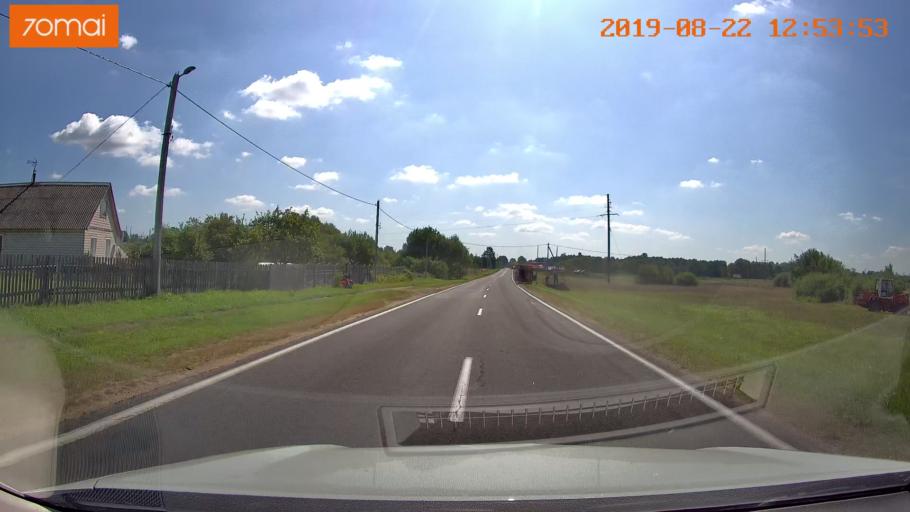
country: BY
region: Minsk
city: Prawdzinski
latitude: 53.4413
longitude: 27.6922
